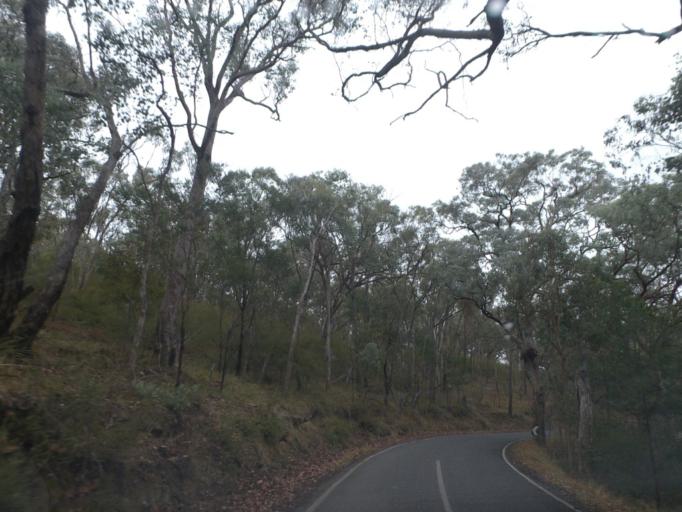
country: AU
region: Victoria
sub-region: Nillumbik
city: Saint Andrews
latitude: -37.6215
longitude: 145.2799
